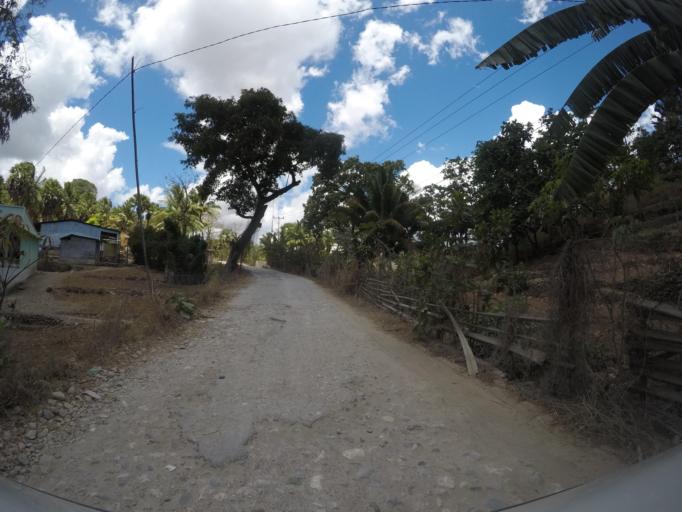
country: TL
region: Baucau
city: Baucau
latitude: -8.4848
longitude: 126.6367
